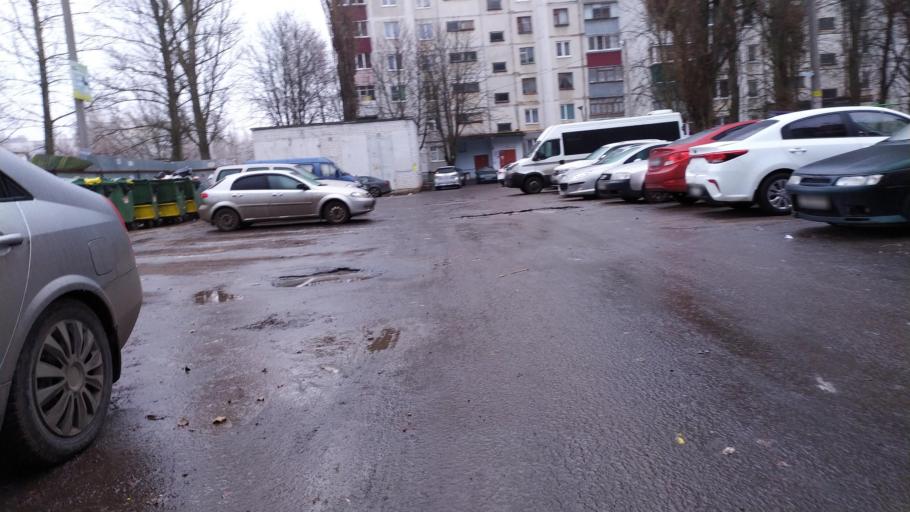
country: RU
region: Kursk
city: Kursk
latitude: 51.7439
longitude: 36.1354
